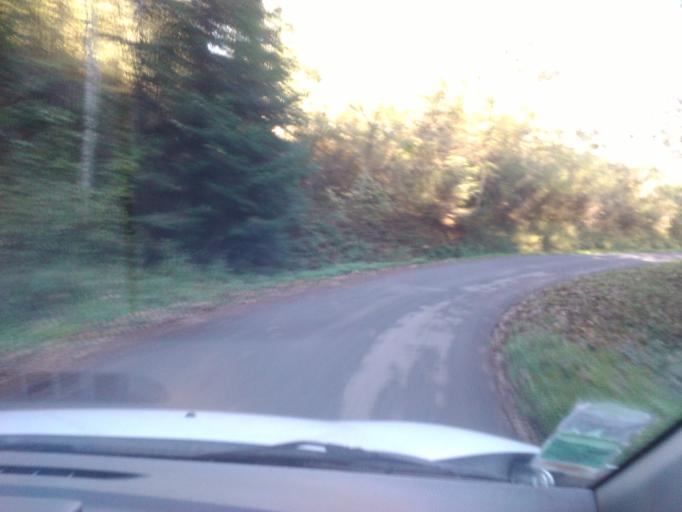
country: FR
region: Lorraine
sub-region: Departement des Vosges
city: Taintrux
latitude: 48.2289
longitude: 6.8824
